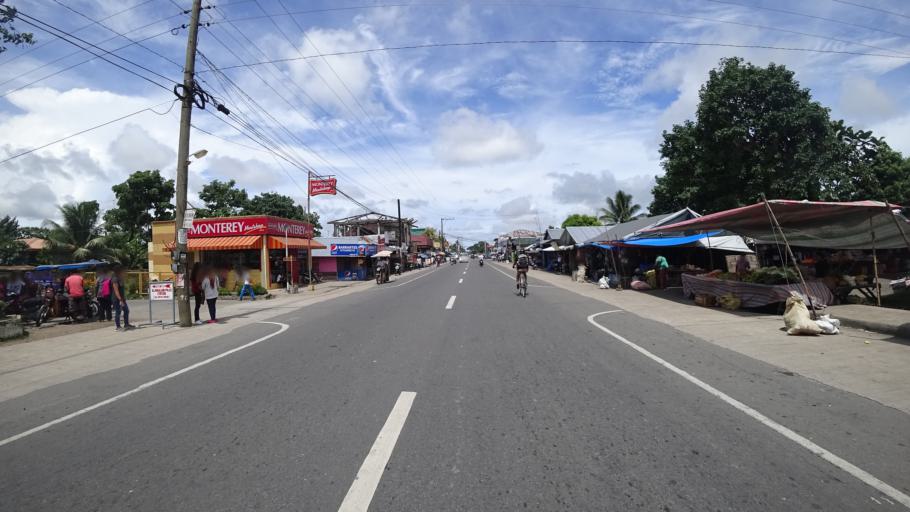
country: PH
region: Eastern Visayas
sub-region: Province of Leyte
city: Alangalang
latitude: 11.2067
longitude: 124.8469
